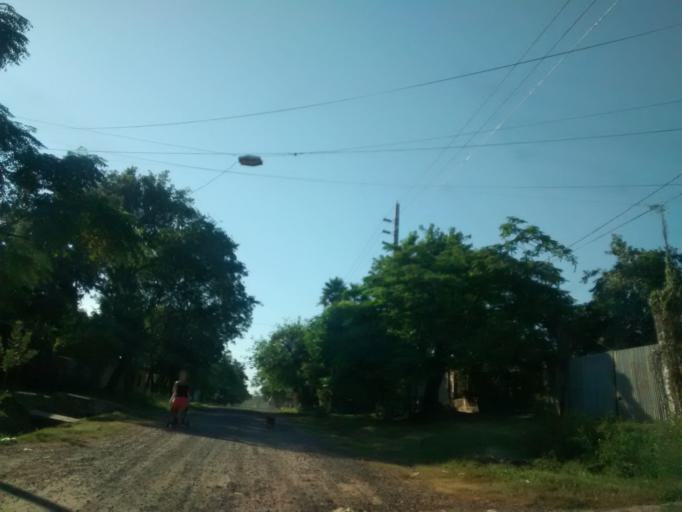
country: AR
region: Chaco
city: Resistencia
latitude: -27.4629
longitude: -58.9681
